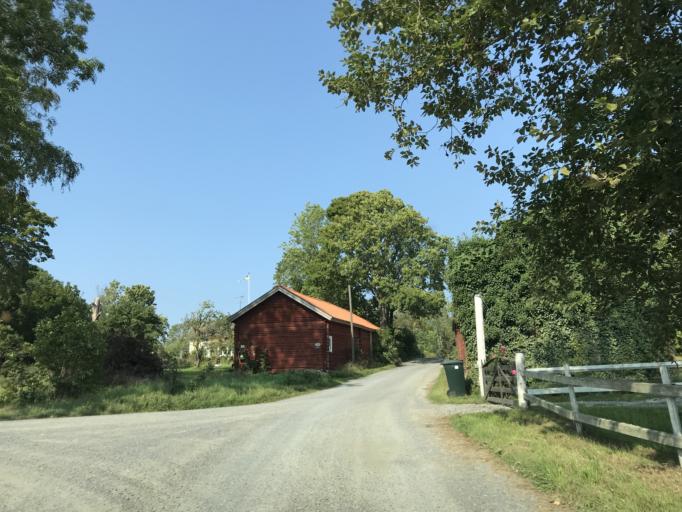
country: SE
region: Stockholm
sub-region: Norrtalje Kommun
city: Bjorko
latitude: 59.8475
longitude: 19.0140
